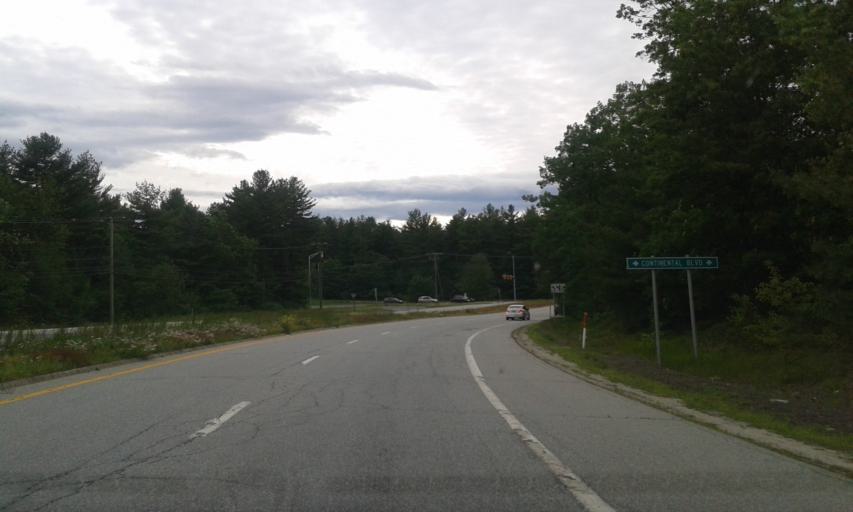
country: US
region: New Hampshire
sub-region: Hillsborough County
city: Litchfield
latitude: 42.8240
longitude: -71.5100
